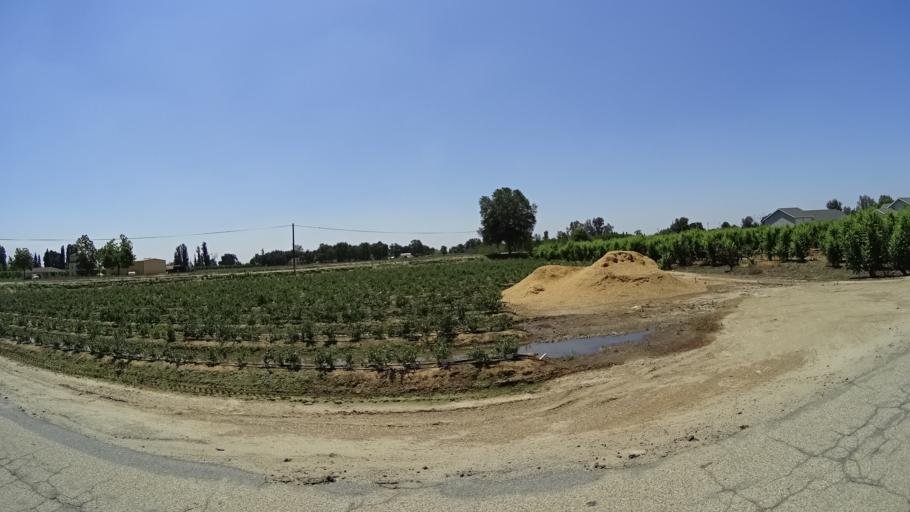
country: US
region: California
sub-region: Fresno County
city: Kingsburg
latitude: 36.4889
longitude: -119.5436
